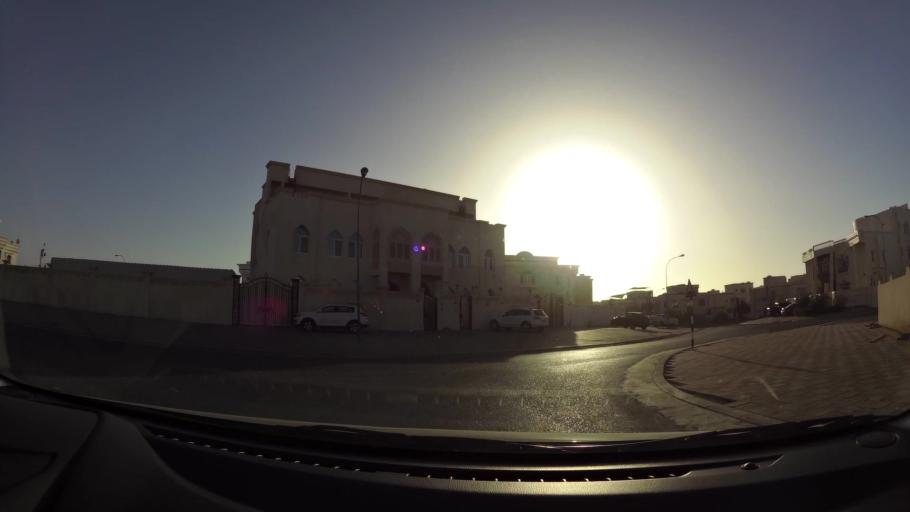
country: OM
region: Muhafazat Masqat
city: As Sib al Jadidah
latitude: 23.6089
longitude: 58.2311
